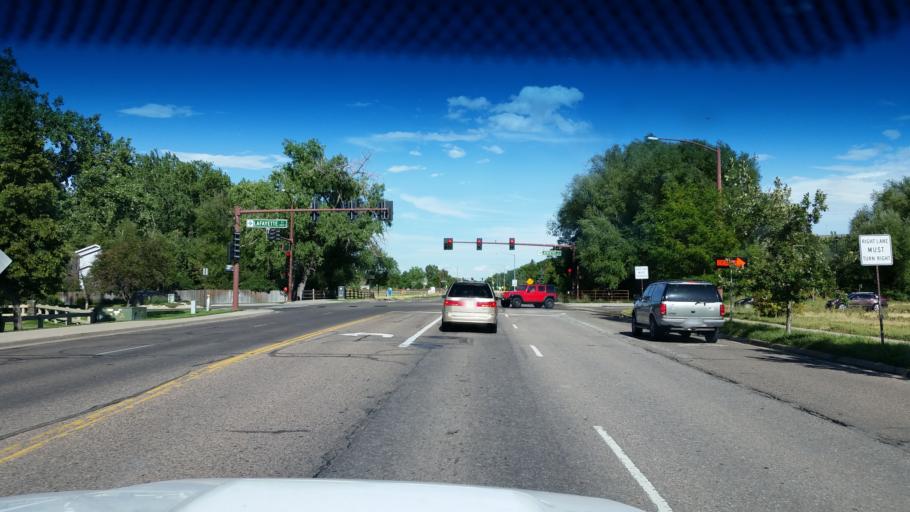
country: US
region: Colorado
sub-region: Adams County
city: Northglenn
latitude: 39.9284
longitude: -104.9696
